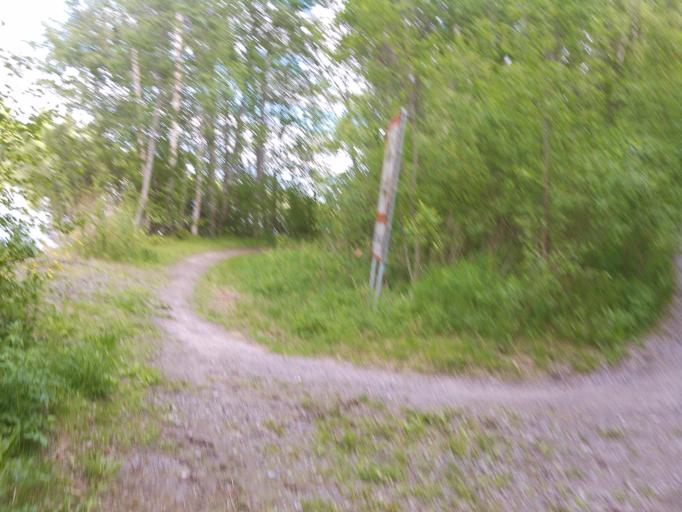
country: SE
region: Vaesterbotten
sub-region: Umea Kommun
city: Roback
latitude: 63.8234
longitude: 20.2039
